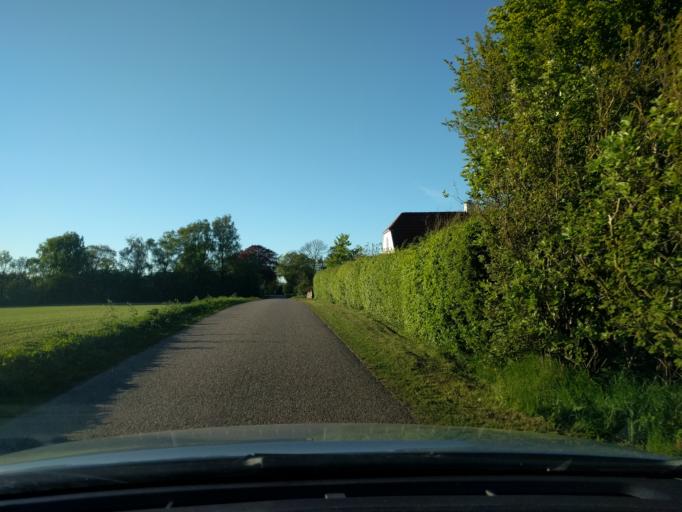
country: DK
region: South Denmark
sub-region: Nyborg Kommune
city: Ullerslev
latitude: 55.3948
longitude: 10.6490
